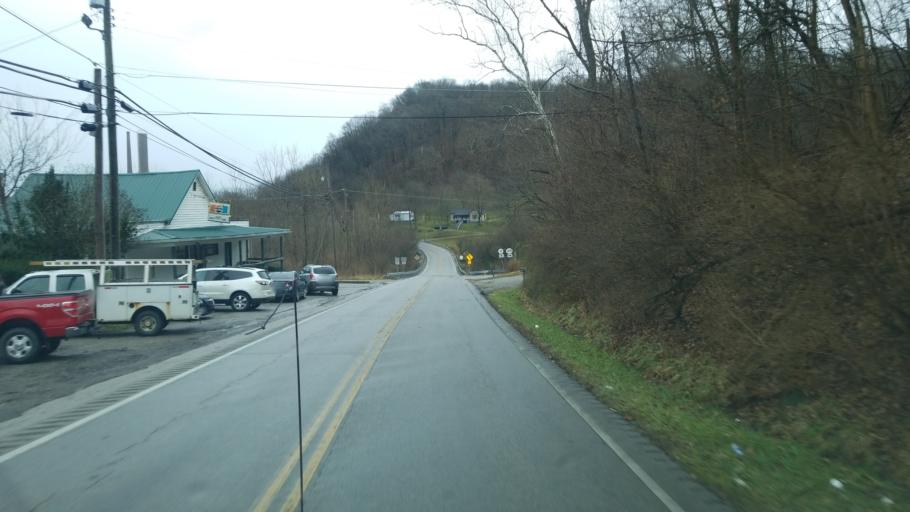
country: US
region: Kentucky
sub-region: Mason County
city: Maysville
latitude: 38.6361
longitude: -83.7183
